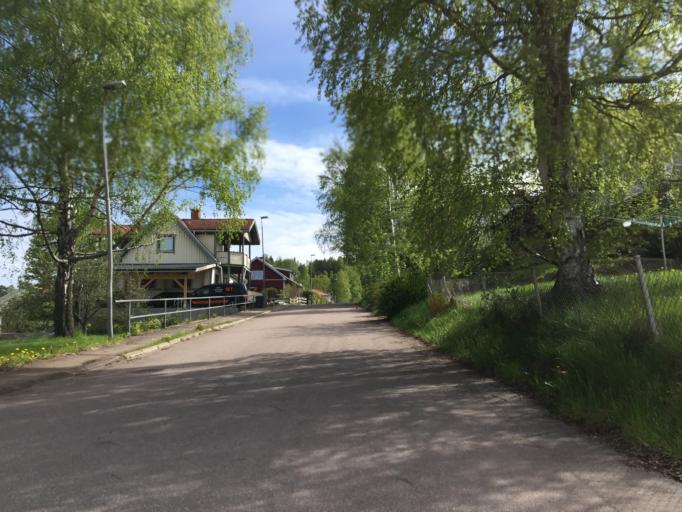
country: SE
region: Dalarna
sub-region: Ludvika Kommun
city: Ludvika
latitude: 60.1361
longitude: 15.1772
